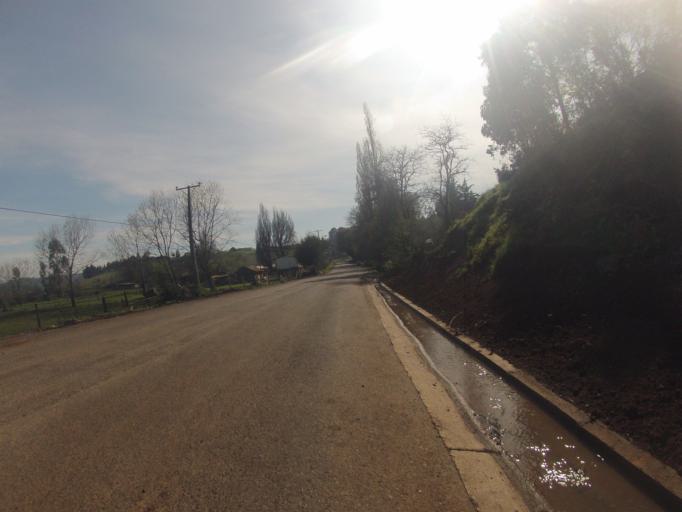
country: CL
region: Araucania
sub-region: Provincia de Cautin
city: Temuco
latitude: -38.7120
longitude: -72.5995
